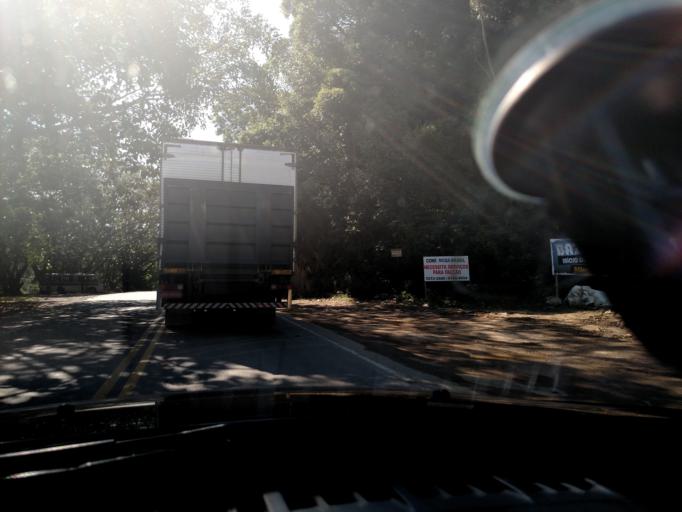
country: BR
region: Santa Catarina
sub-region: Ibirama
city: Ibirama
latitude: -27.0933
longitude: -49.4682
